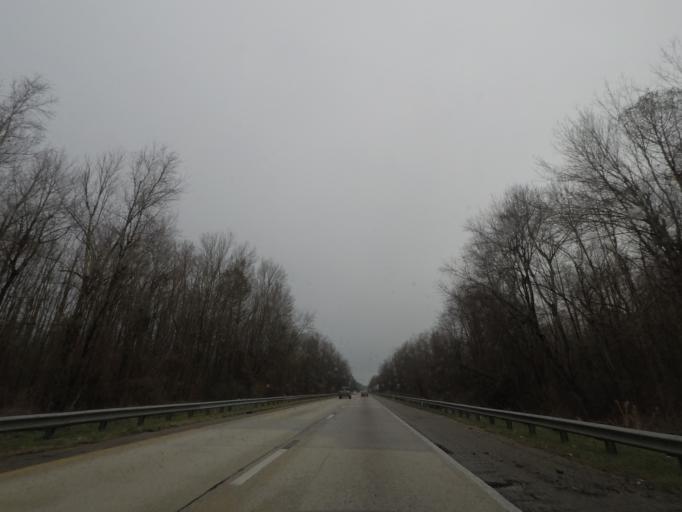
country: US
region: South Carolina
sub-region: Clarendon County
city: Manning
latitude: 33.7328
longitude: -80.2188
